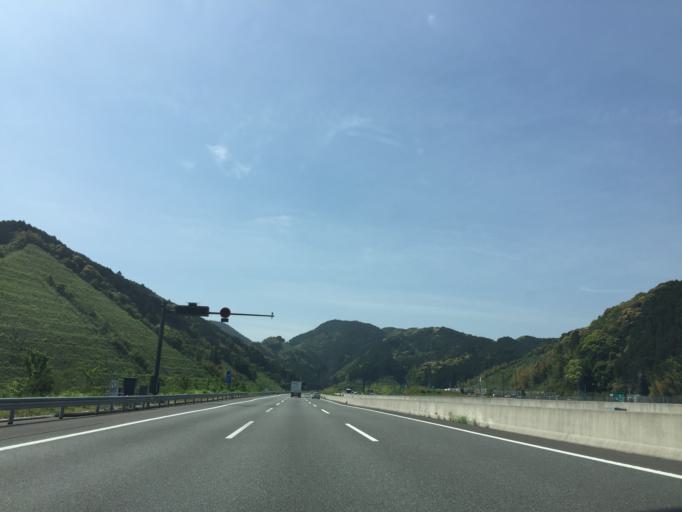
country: JP
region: Shizuoka
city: Shizuoka-shi
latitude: 34.9729
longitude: 138.2930
